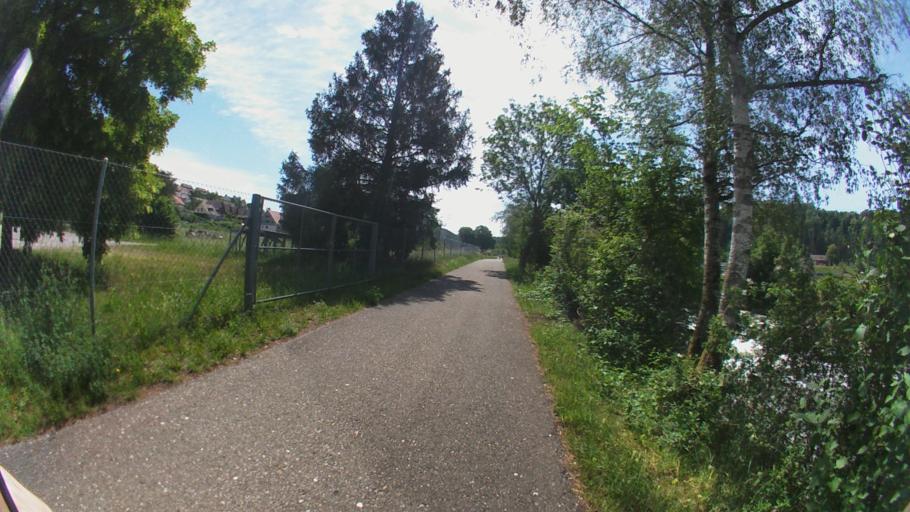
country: CH
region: Zurich
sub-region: Bezirk Buelach
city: Glattfelden
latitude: 47.5621
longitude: 8.4926
